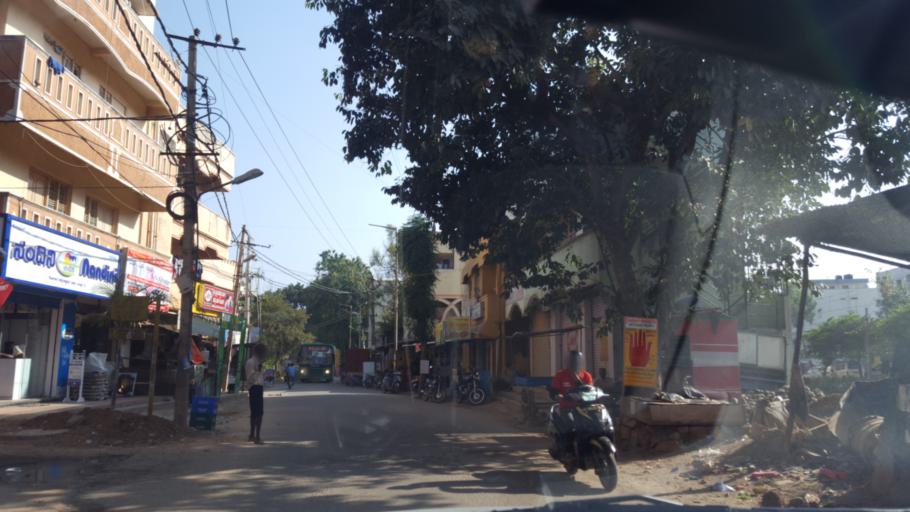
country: IN
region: Karnataka
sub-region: Bangalore Urban
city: Bangalore
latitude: 12.9543
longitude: 77.7051
